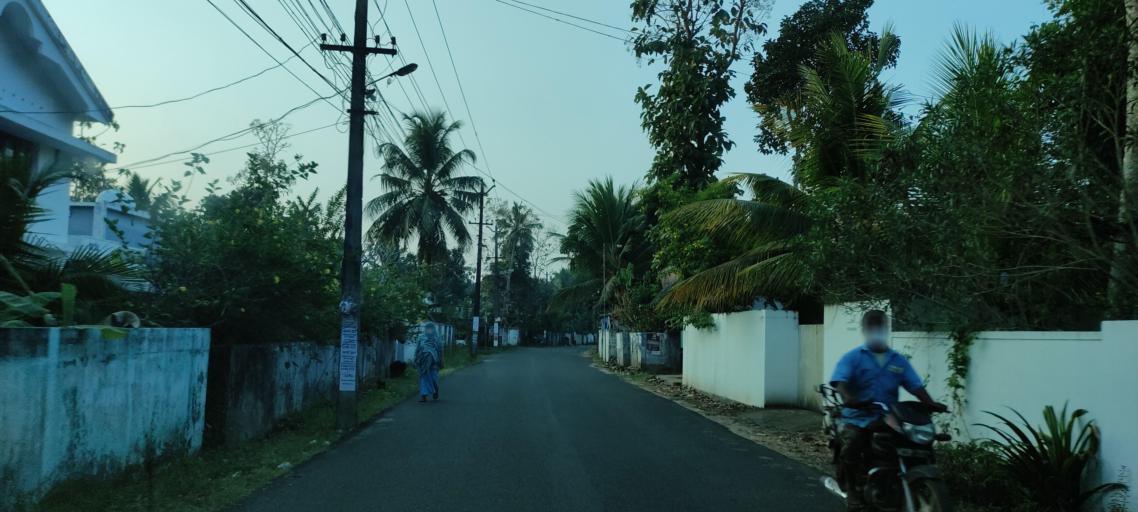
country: IN
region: Kerala
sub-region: Alappuzha
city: Alleppey
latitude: 9.4334
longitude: 76.3482
